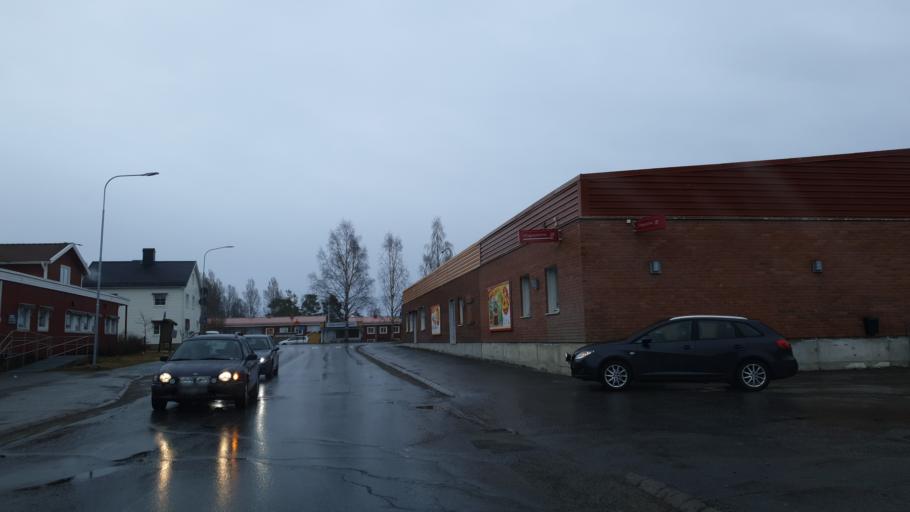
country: SE
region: Vaesterbotten
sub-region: Skelleftea Kommun
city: Kage
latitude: 64.8323
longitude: 20.9873
